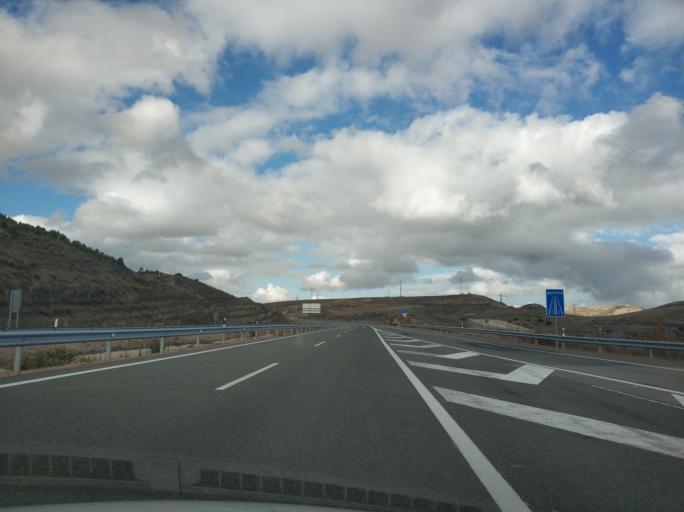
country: ES
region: Castille and Leon
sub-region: Provincia de Soria
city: Yelo
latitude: 41.2210
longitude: -2.4721
